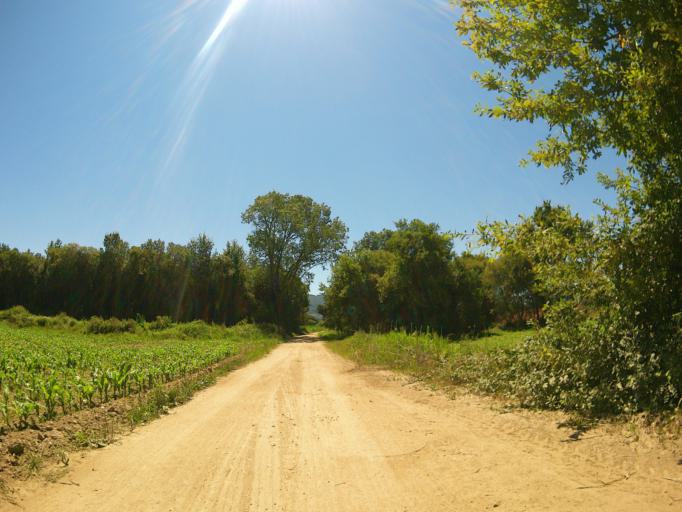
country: PT
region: Viana do Castelo
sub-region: Viana do Castelo
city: Darque
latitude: 41.7211
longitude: -8.7061
